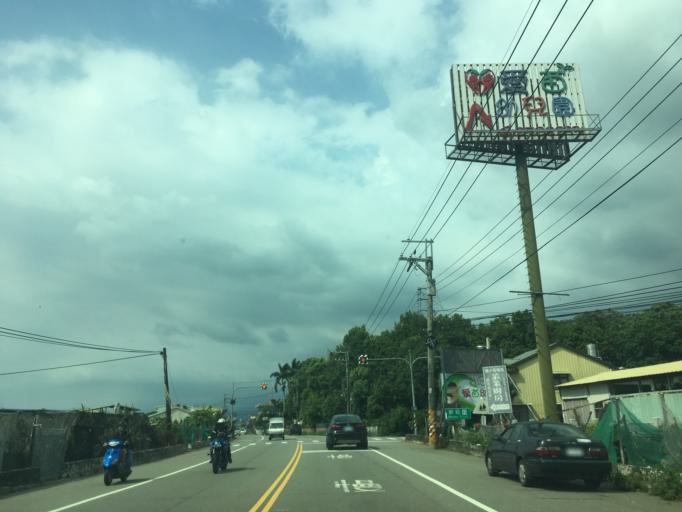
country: TW
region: Taiwan
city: Fengyuan
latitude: 24.2361
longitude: 120.8049
